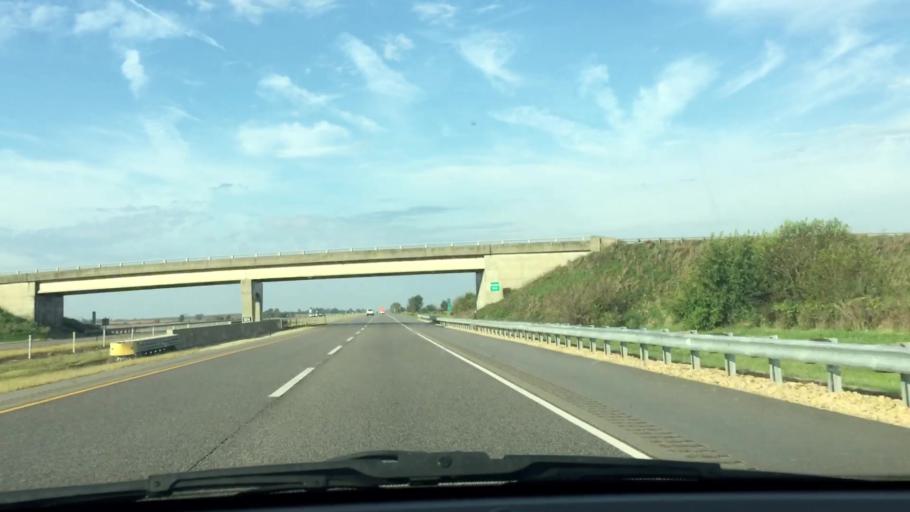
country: US
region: Illinois
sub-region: Ogle County
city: Rochelle
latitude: 41.8697
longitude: -89.1676
